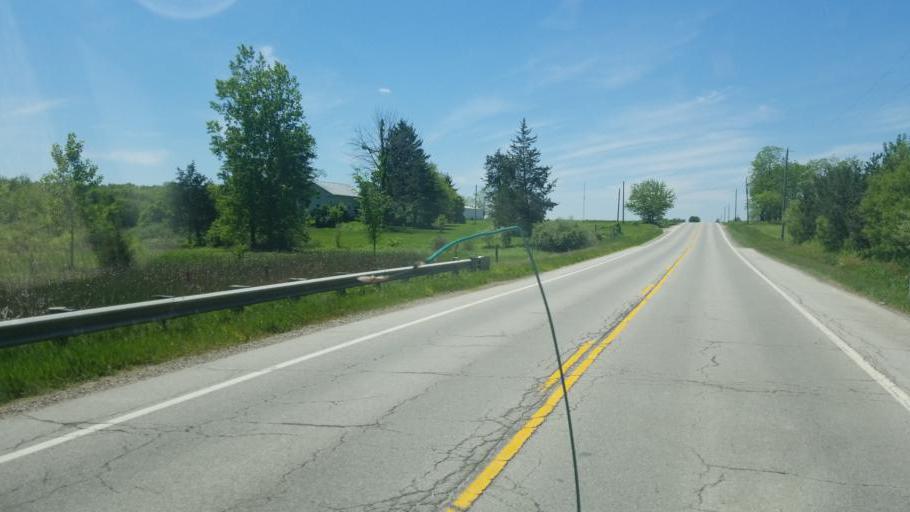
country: US
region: Ohio
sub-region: Huron County
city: Greenwich
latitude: 41.0294
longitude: -82.4553
